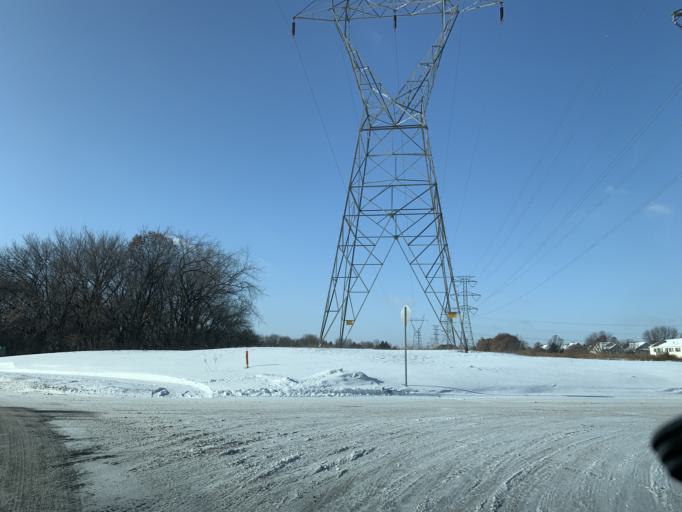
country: US
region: Minnesota
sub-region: Scott County
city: Prior Lake
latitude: 44.7778
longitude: -93.4182
